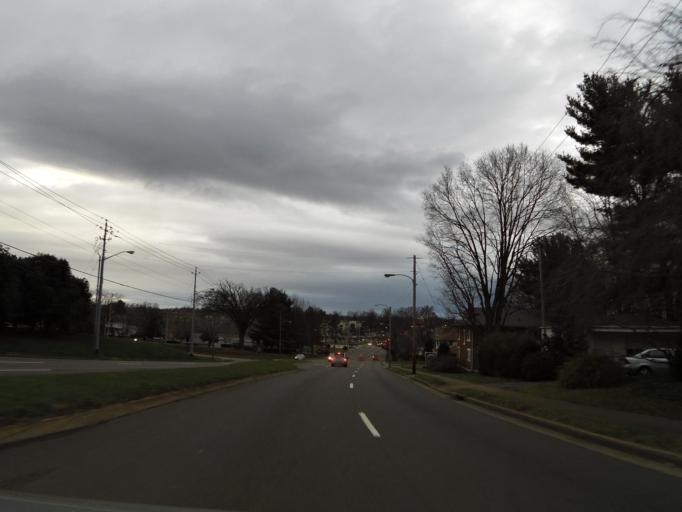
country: US
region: Tennessee
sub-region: Washington County
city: Johnson City
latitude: 36.3046
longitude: -82.3630
